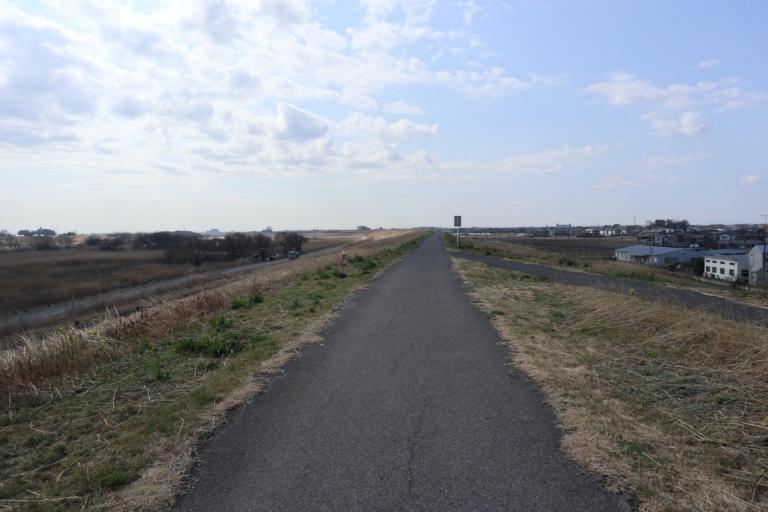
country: JP
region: Ibaraki
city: Koga
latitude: 36.1845
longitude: 139.6894
